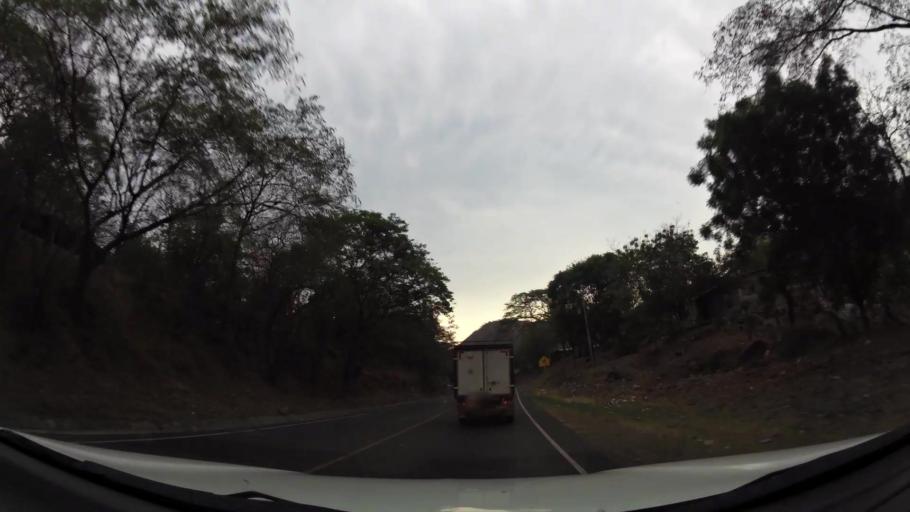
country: NI
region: Esteli
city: Esteli
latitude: 12.9492
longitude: -86.2230
